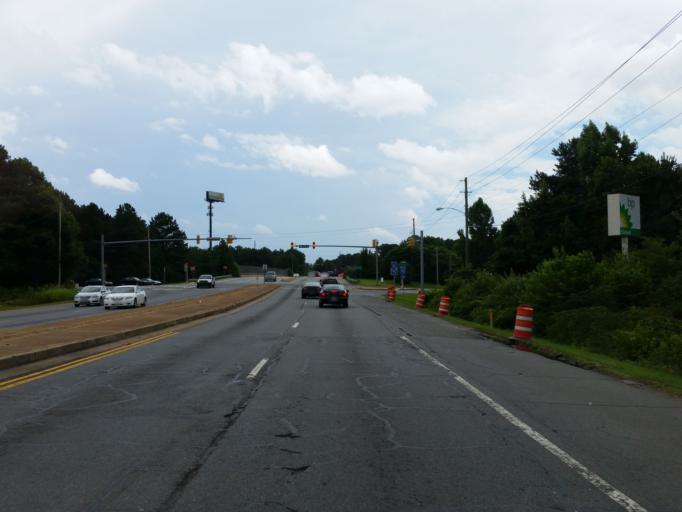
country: US
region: Georgia
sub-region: Cobb County
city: Kennesaw
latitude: 34.0560
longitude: -84.5933
